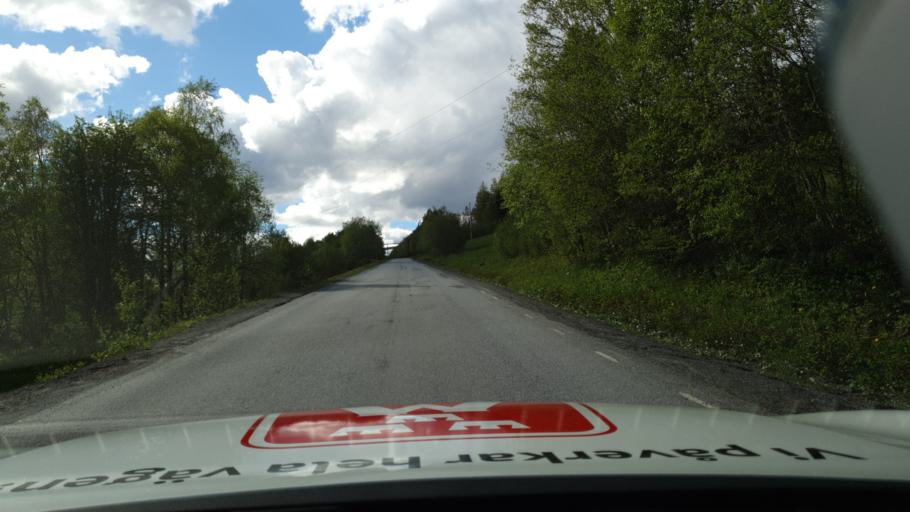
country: SE
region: Jaemtland
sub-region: Are Kommun
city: Are
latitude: 63.4060
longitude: 13.0359
